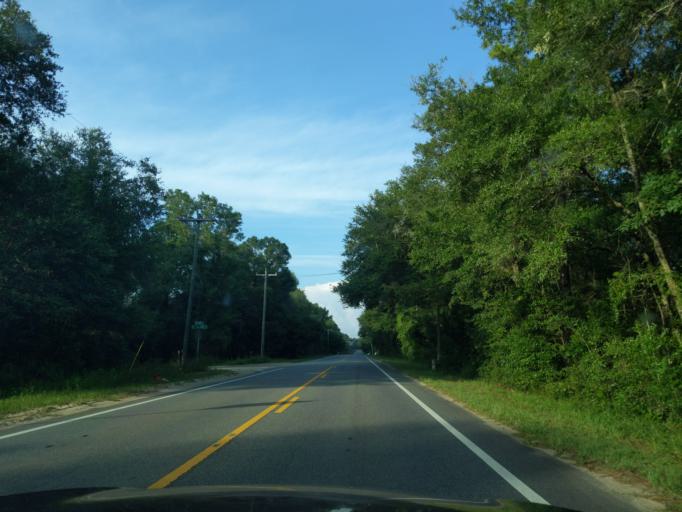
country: US
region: Florida
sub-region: Leon County
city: Tallahassee
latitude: 30.3745
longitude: -84.3587
